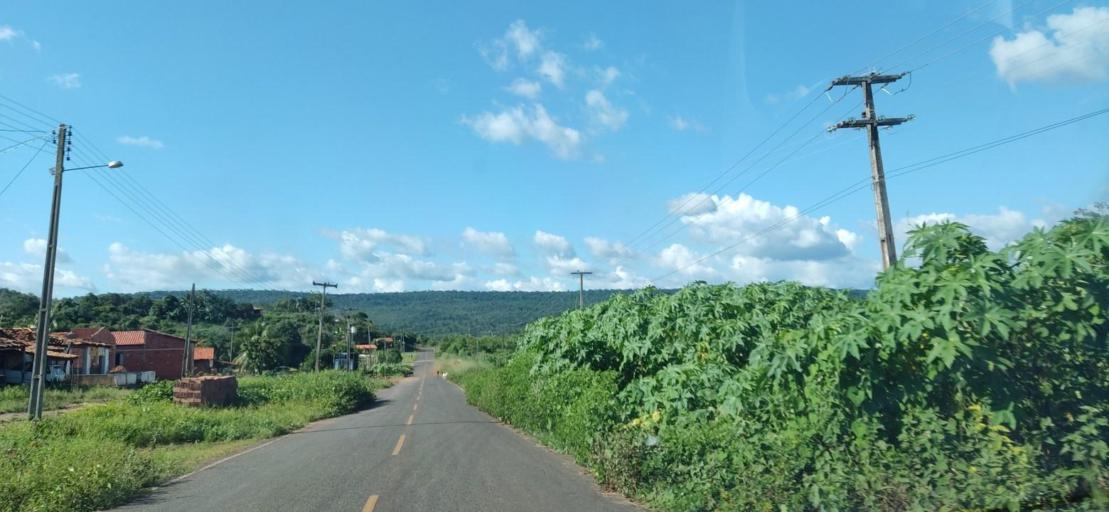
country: BR
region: Piaui
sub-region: Valenca Do Piaui
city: Valenca do Piaui
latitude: -6.1763
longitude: -41.8186
